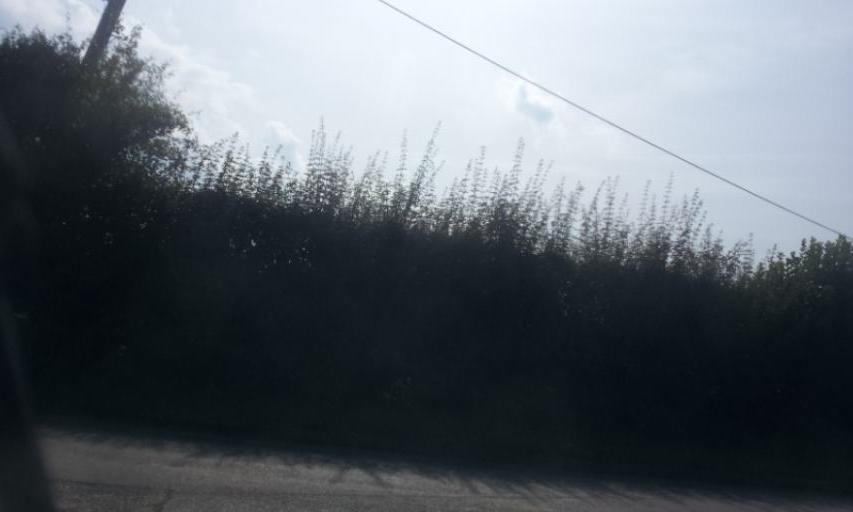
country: GB
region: England
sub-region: Kent
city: Paddock Wood
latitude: 51.1691
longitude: 0.4002
